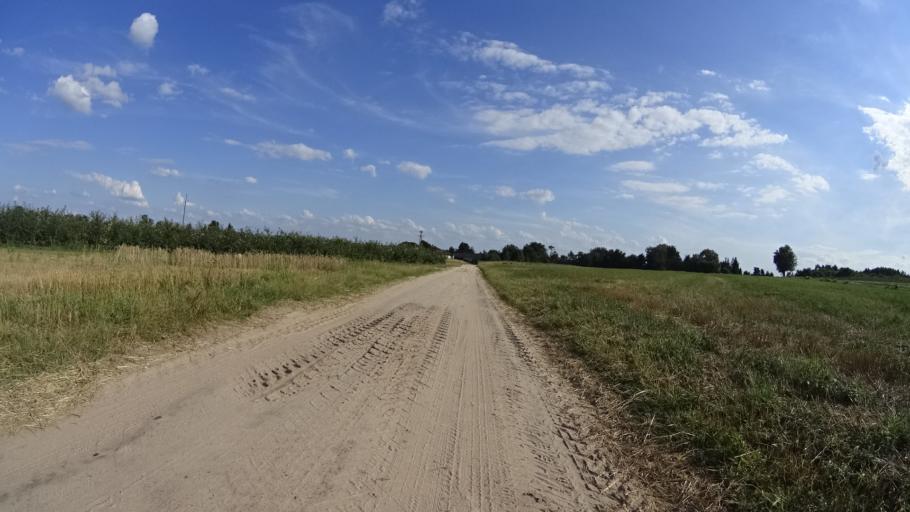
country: PL
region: Masovian Voivodeship
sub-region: Powiat bialobrzeski
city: Wysmierzyce
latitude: 51.6588
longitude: 20.8214
